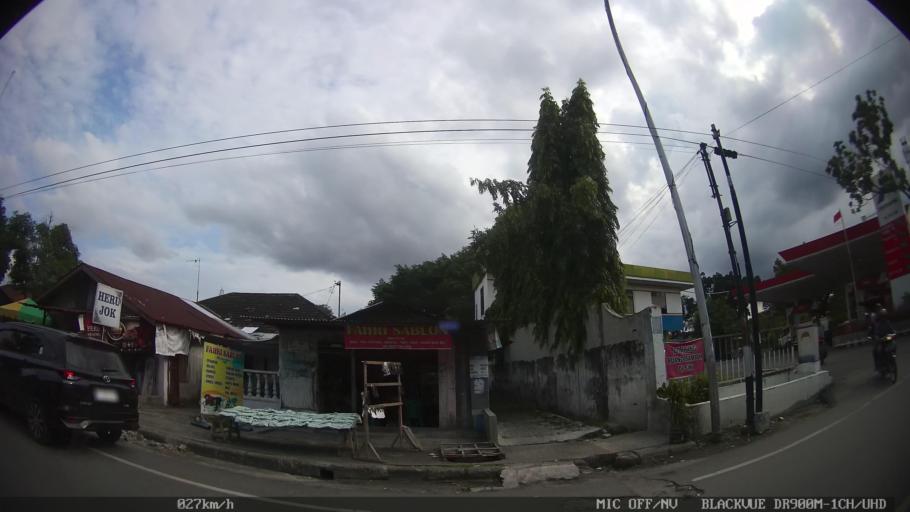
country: ID
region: North Sumatra
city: Medan
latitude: 3.5989
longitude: 98.6838
